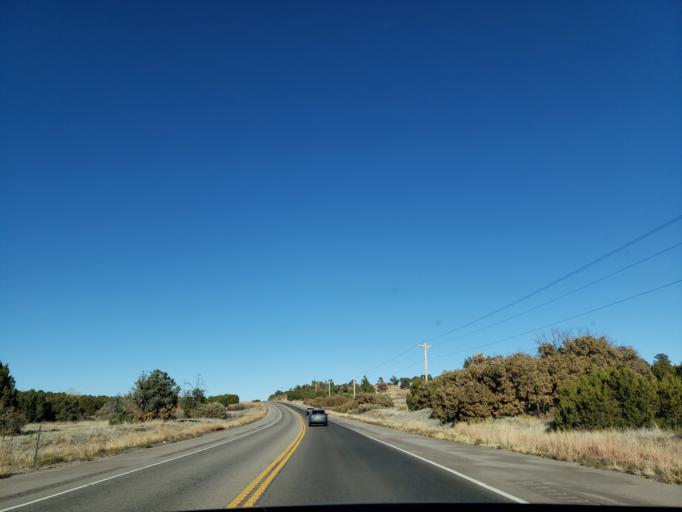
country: US
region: Colorado
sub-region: Fremont County
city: Penrose
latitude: 38.5839
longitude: -104.9197
